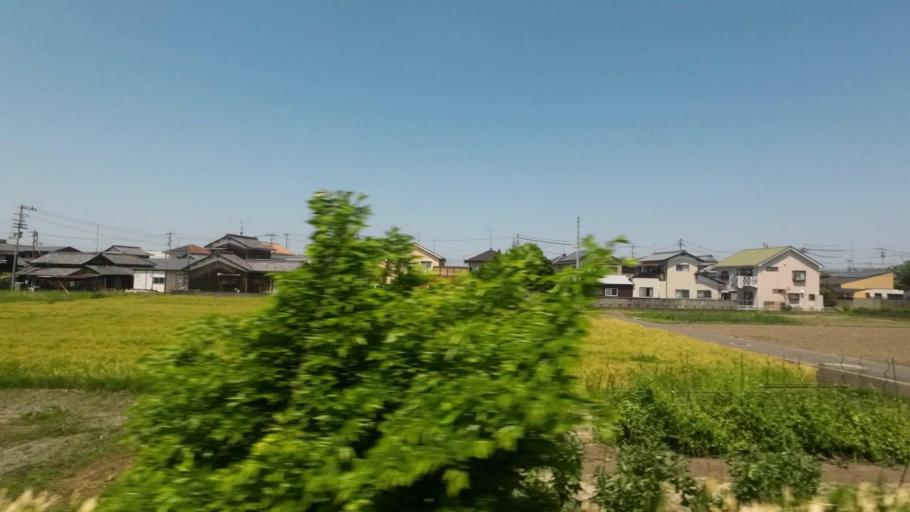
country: JP
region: Ehime
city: Hojo
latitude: 33.9395
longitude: 132.7690
